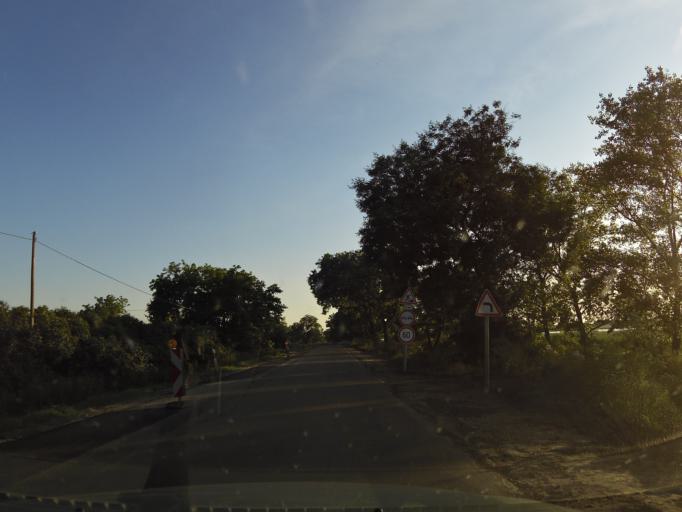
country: HU
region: Csongrad
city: Szentes
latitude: 46.6825
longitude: 20.3175
